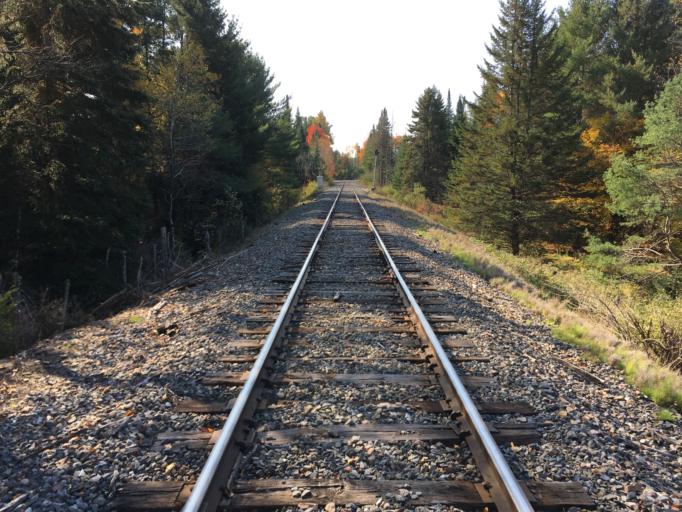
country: US
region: Vermont
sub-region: Caledonia County
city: Lyndonville
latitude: 44.6093
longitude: -71.9680
